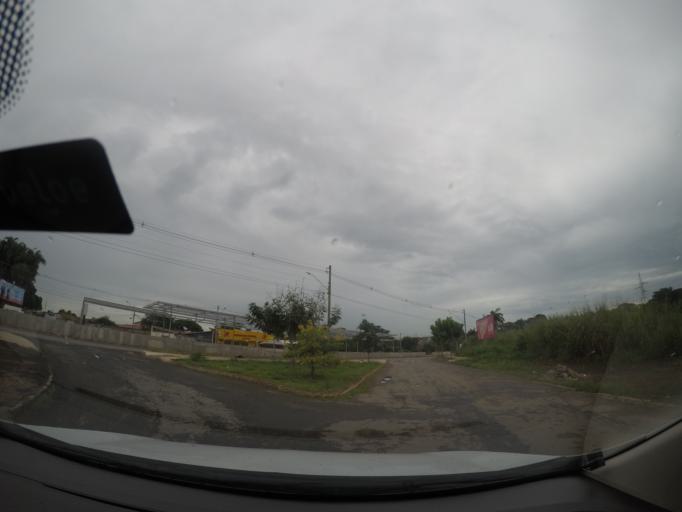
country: BR
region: Goias
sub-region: Goiania
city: Goiania
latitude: -16.6455
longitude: -49.2658
